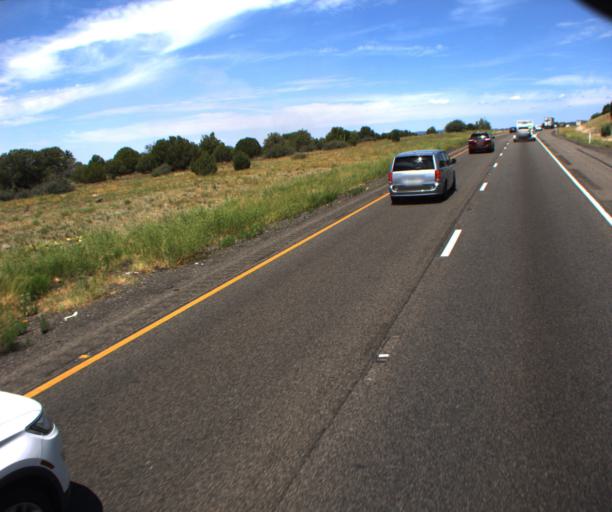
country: US
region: Arizona
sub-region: Yavapai County
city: Village of Oak Creek (Big Park)
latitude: 34.8002
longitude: -111.5928
